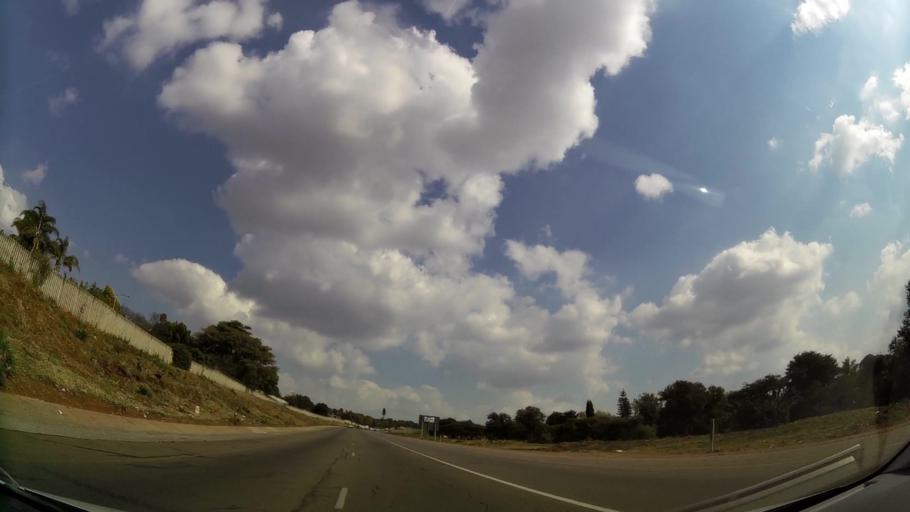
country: ZA
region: Gauteng
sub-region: City of Tshwane Metropolitan Municipality
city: Centurion
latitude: -25.8057
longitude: 28.2930
